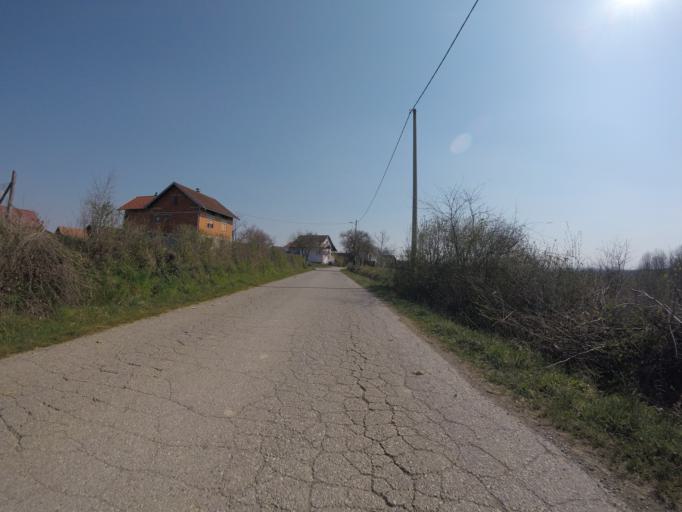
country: HR
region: Grad Zagreb
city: Strmec
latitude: 45.5722
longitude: 15.9222
